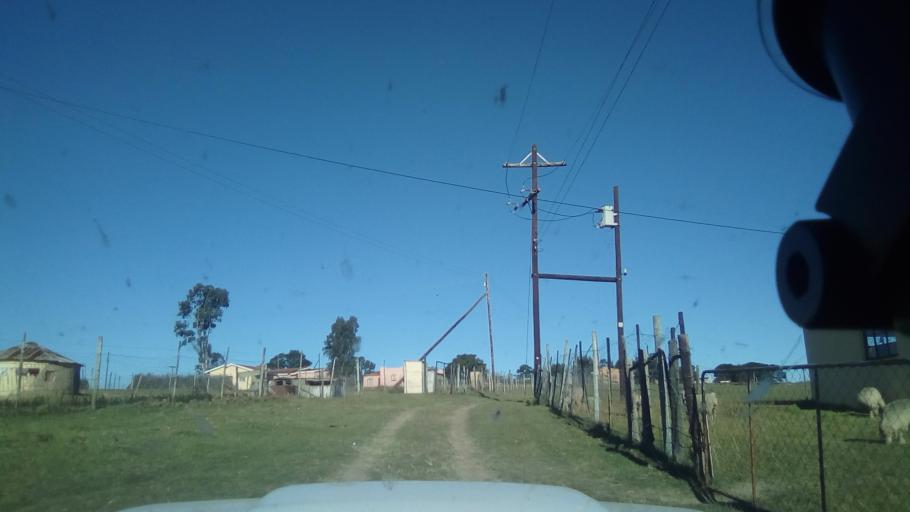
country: ZA
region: Eastern Cape
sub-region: Buffalo City Metropolitan Municipality
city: Bhisho
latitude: -32.9494
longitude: 27.2908
